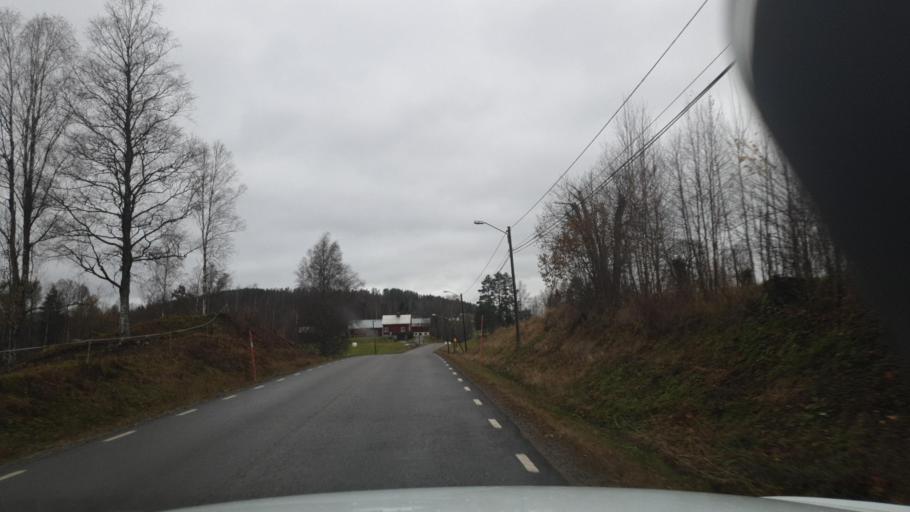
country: SE
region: Vaermland
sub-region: Eda Kommun
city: Charlottenberg
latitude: 59.9288
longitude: 12.5208
